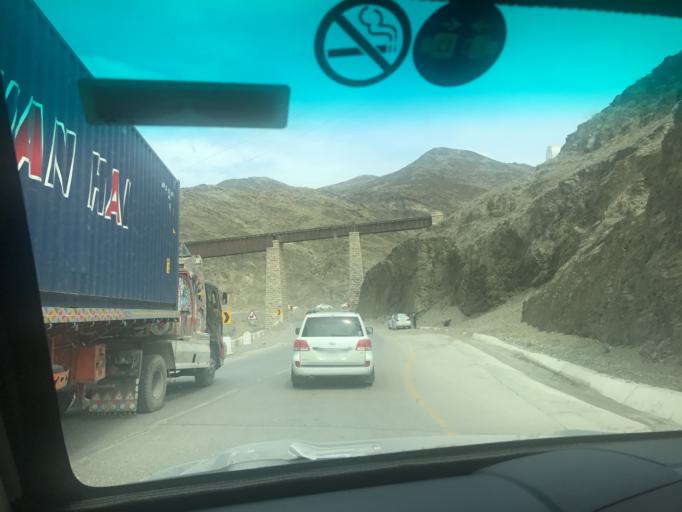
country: PK
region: Federally Administered Tribal Areas
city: Landi Kotal
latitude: 34.1038
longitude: 71.1314
